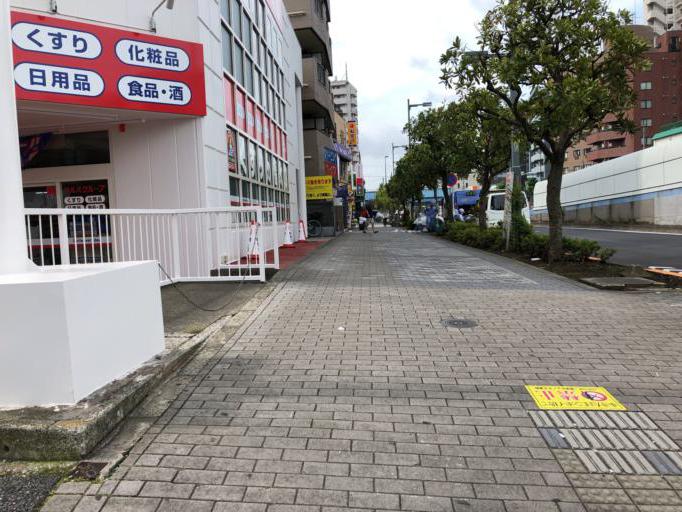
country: JP
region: Tokyo
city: Urayasu
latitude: 35.6663
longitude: 139.8735
